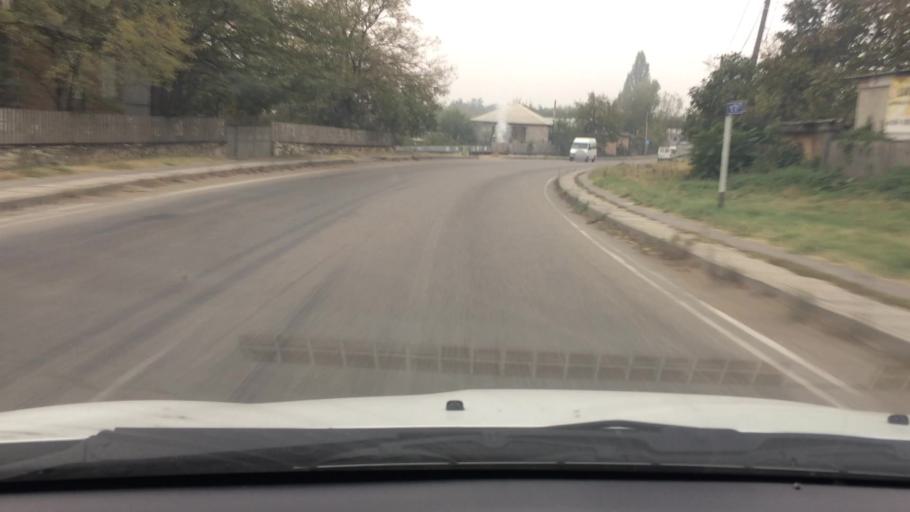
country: GE
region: Kvemo Kartli
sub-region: Marneuli
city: Marneuli
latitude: 41.5819
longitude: 44.7766
